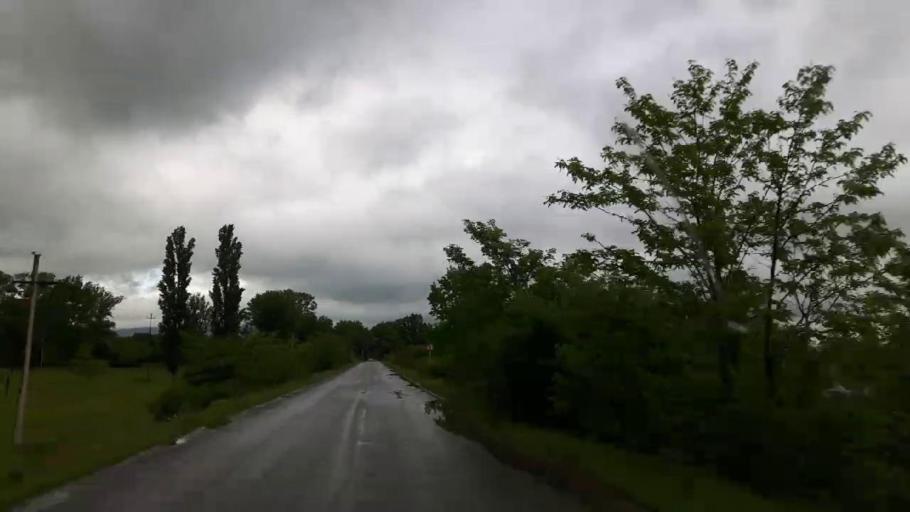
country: GE
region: Shida Kartli
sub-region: Khashuris Raioni
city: Khashuri
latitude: 41.9943
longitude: 43.6570
